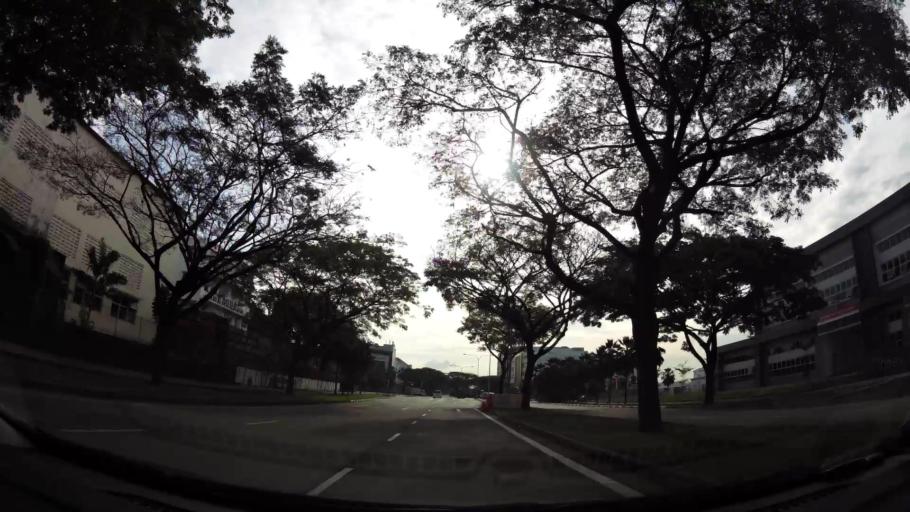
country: MY
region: Johor
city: Johor Bahru
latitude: 1.2904
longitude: 103.6245
